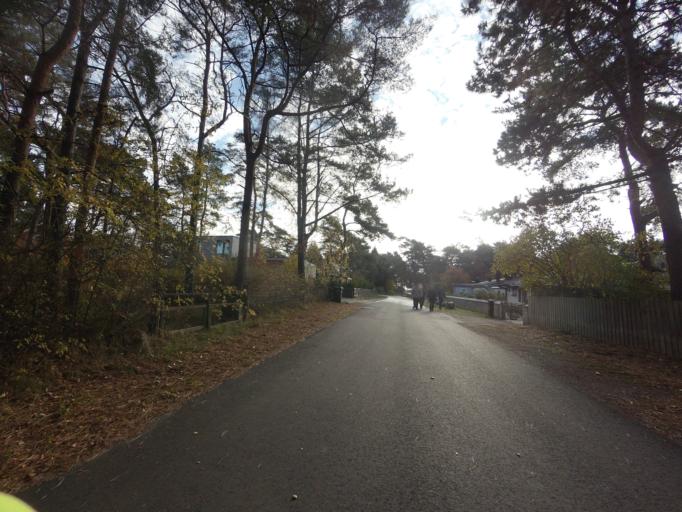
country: SE
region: Skane
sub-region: Vellinge Kommun
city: Hollviken
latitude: 55.4037
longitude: 12.9727
